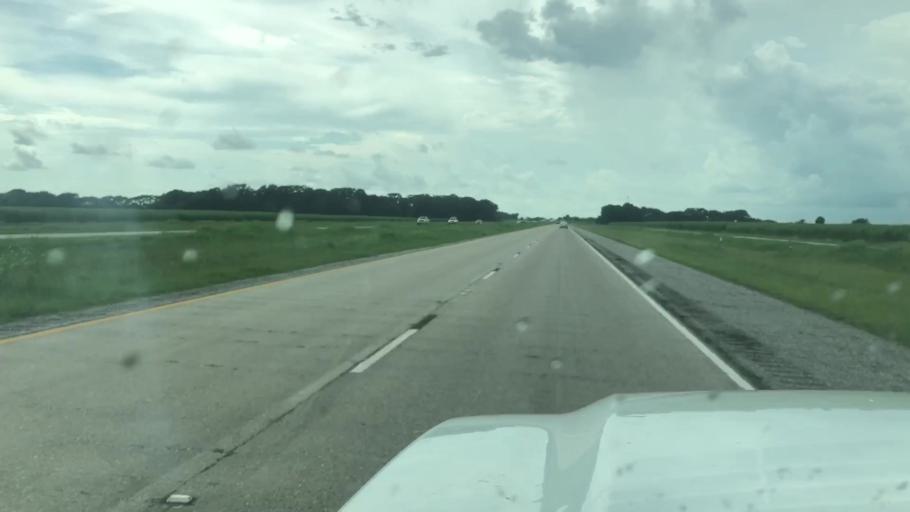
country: US
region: Louisiana
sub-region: Saint Mary Parish
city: Baldwin
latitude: 29.8538
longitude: -91.6042
